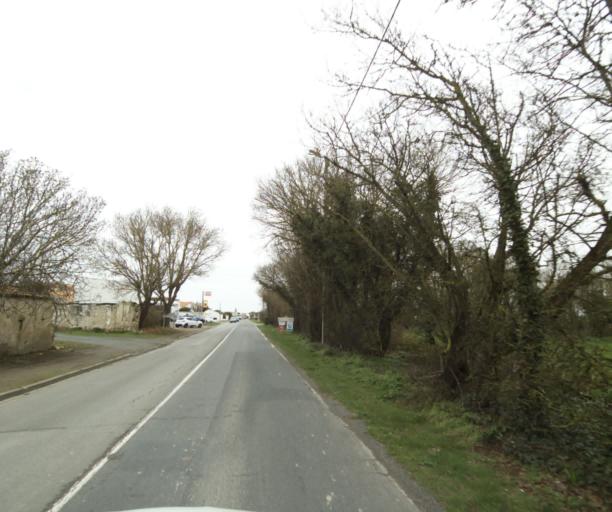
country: FR
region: Poitou-Charentes
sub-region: Departement de la Charente-Maritime
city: Nieul-sur-Mer
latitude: 46.1978
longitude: -1.1580
